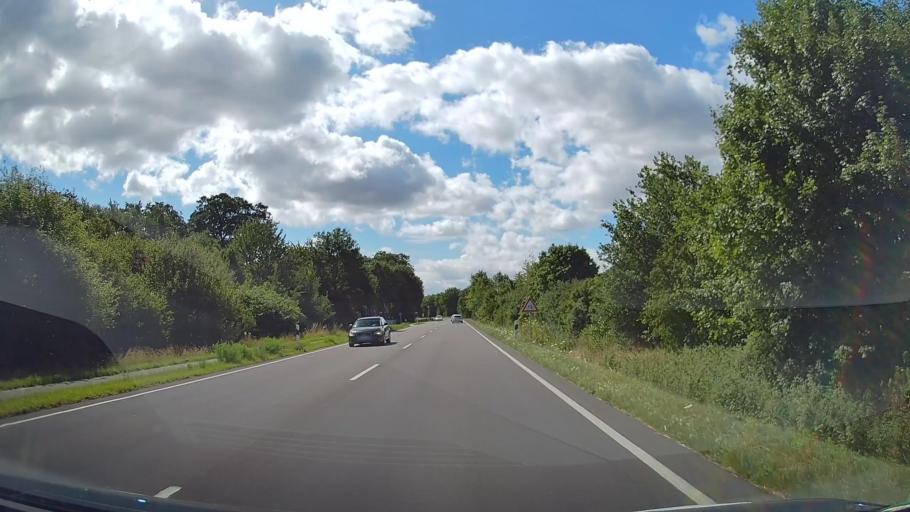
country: DE
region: Lower Saxony
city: Vechta
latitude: 52.6963
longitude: 8.3032
